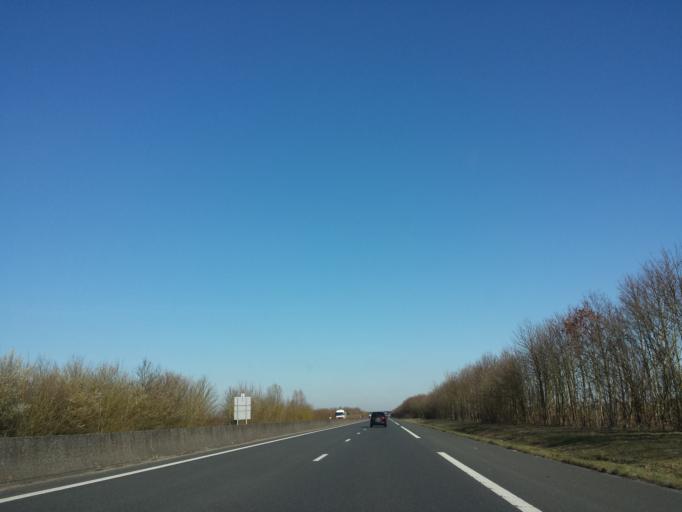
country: FR
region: Picardie
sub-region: Departement de l'Oise
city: Tille
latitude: 49.4746
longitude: 2.1631
